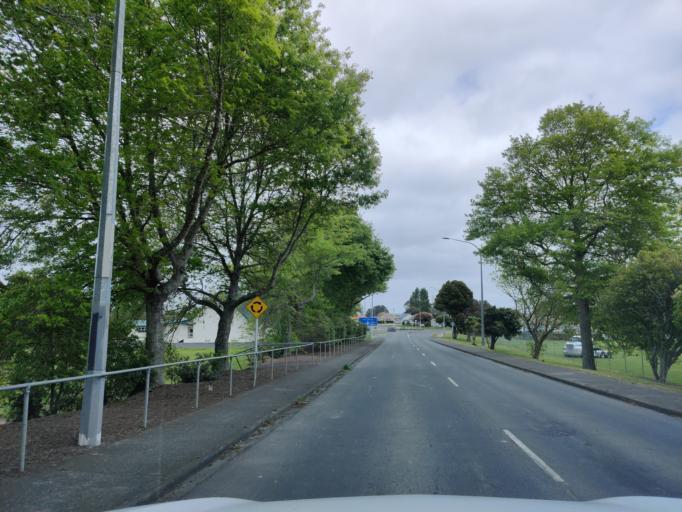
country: NZ
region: Waikato
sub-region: Waikato District
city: Ngaruawahia
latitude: -37.5660
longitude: 175.1531
